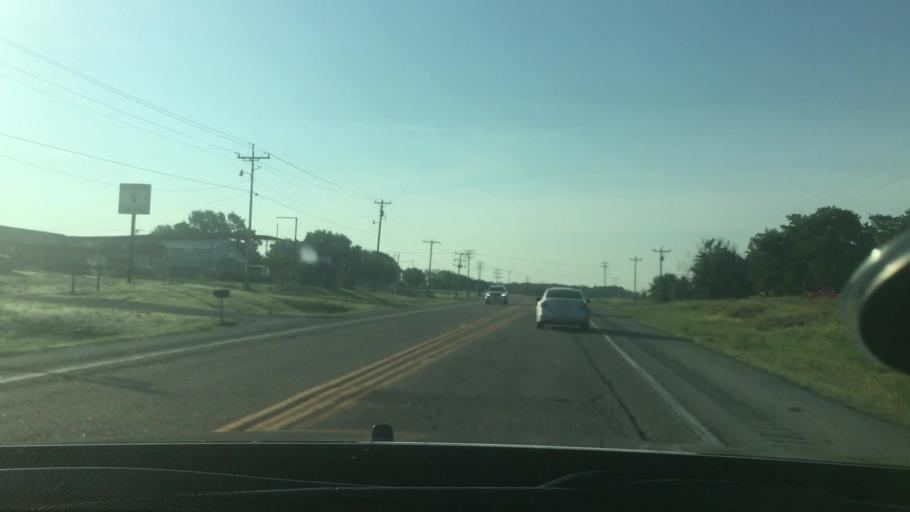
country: US
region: Oklahoma
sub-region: Pontotoc County
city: Ada
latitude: 34.8012
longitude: -96.7416
